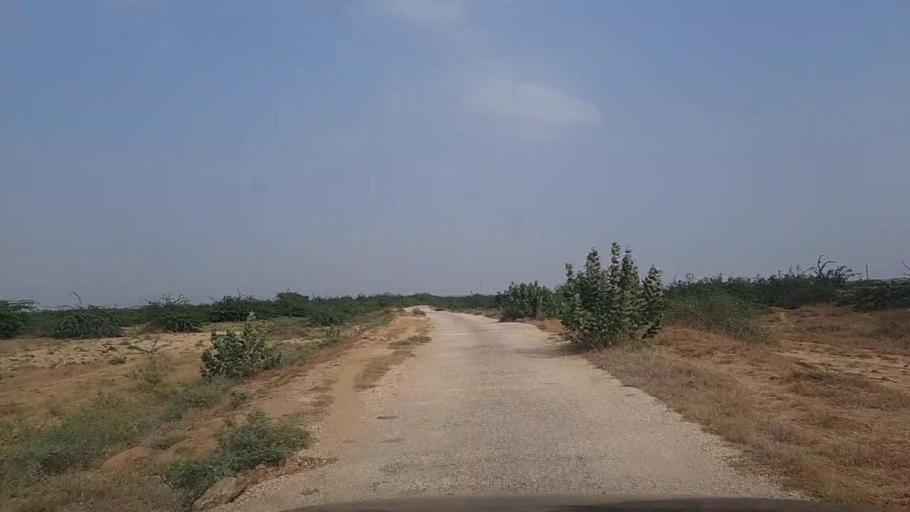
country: PK
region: Sindh
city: Thatta
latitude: 24.8603
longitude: 67.7865
